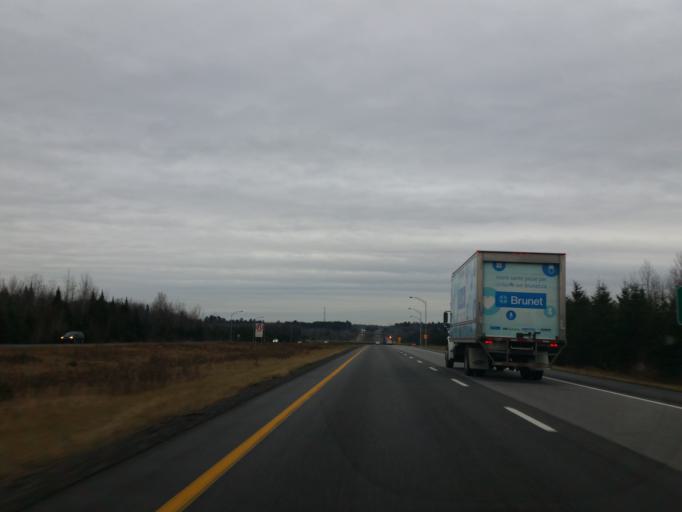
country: CA
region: Quebec
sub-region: Capitale-Nationale
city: Cap-Sante
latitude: 46.6969
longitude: -71.9017
